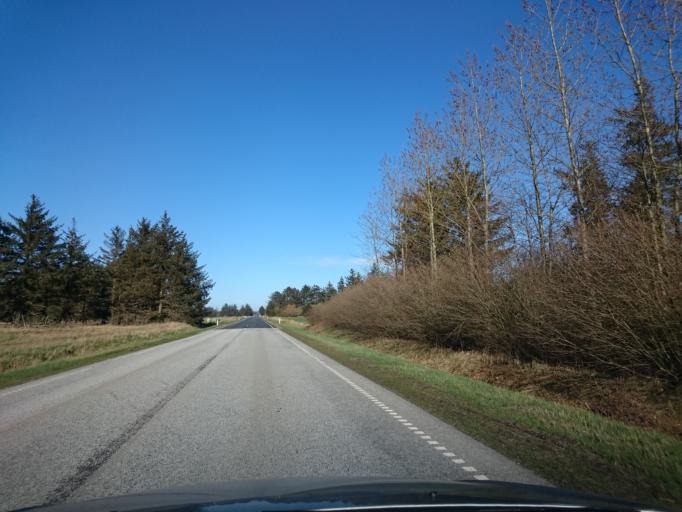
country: DK
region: North Denmark
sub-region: Hjorring Kommune
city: Sindal
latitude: 57.5911
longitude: 10.2921
